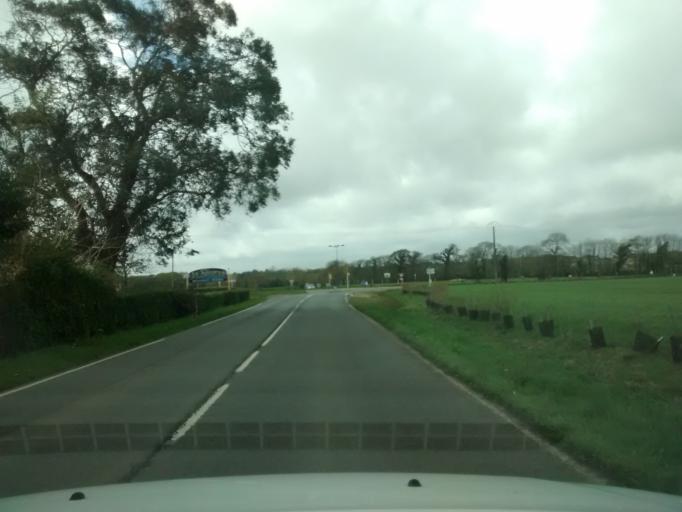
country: FR
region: Brittany
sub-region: Departement du Finistere
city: Clohars-Carnoet
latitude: 47.8000
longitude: -3.5539
